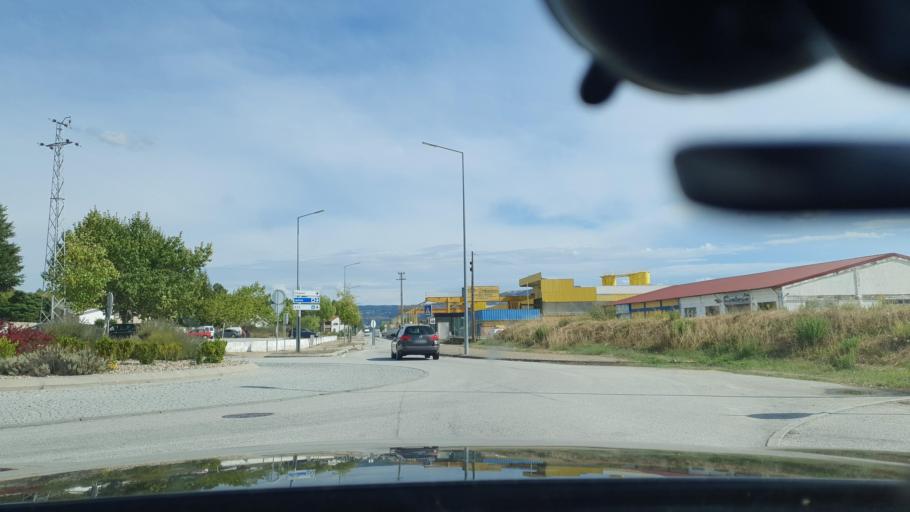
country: PT
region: Vila Real
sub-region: Chaves
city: Chaves
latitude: 41.7693
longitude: -7.4850
